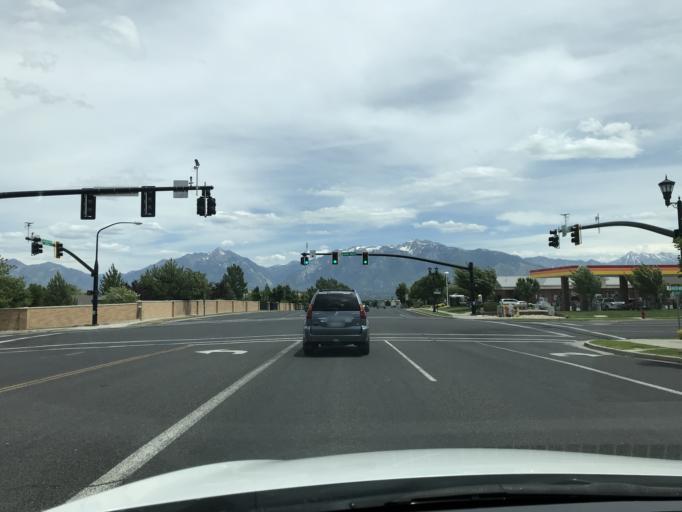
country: US
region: Utah
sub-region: Salt Lake County
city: South Jordan Heights
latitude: 40.5623
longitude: -111.9868
